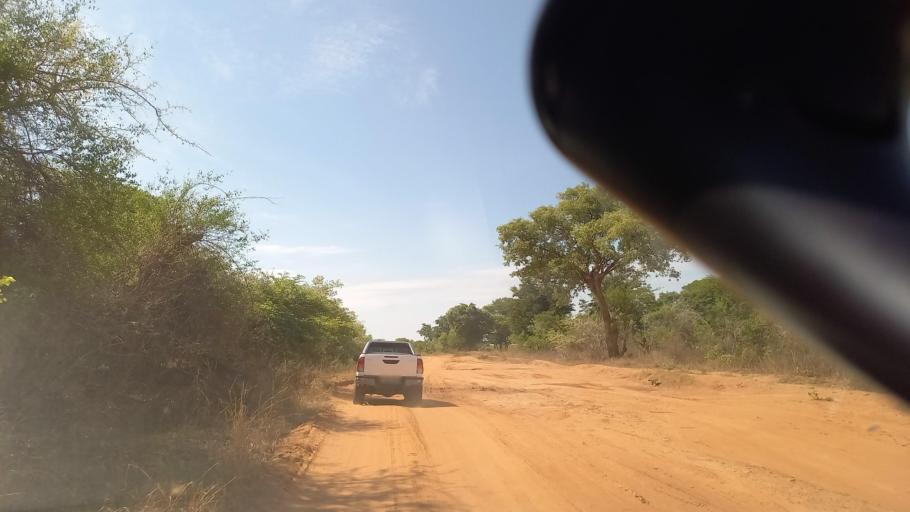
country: ZM
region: Southern
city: Mazabuka
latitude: -16.0370
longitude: 27.6177
